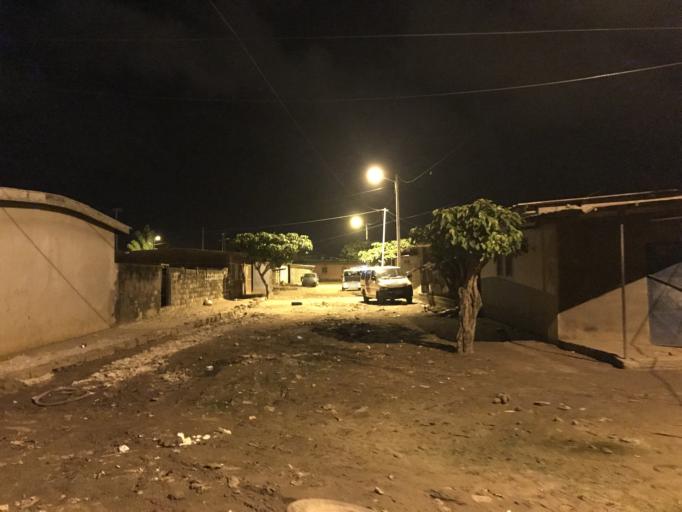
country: CI
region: Sud-Comoe
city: Grand-Bassam
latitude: 5.2124
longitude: -3.7337
